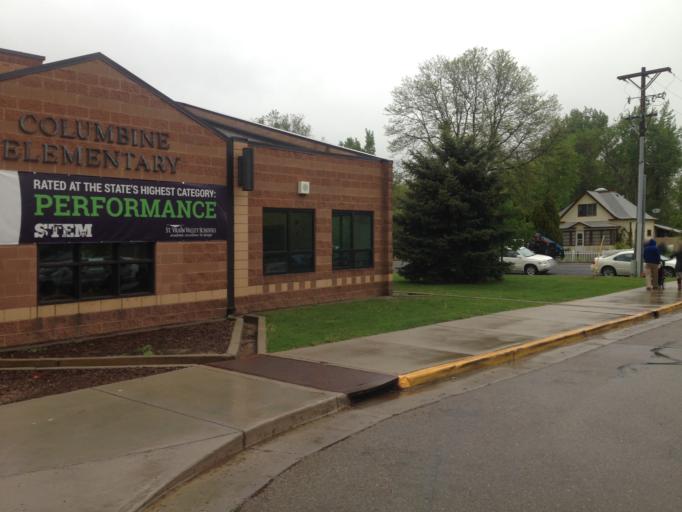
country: US
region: Colorado
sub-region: Boulder County
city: Longmont
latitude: 40.1703
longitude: -105.0955
